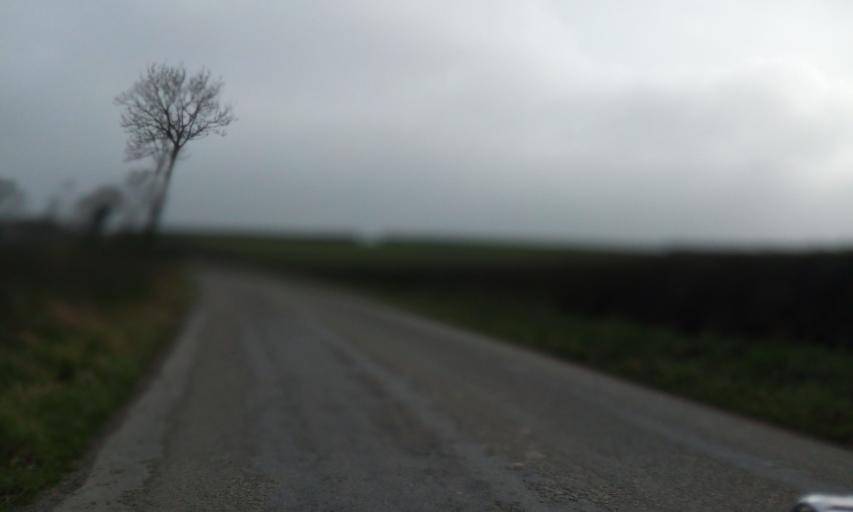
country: IE
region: Leinster
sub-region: Kilkenny
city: Kilkenny
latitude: 52.6576
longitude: -7.1807
